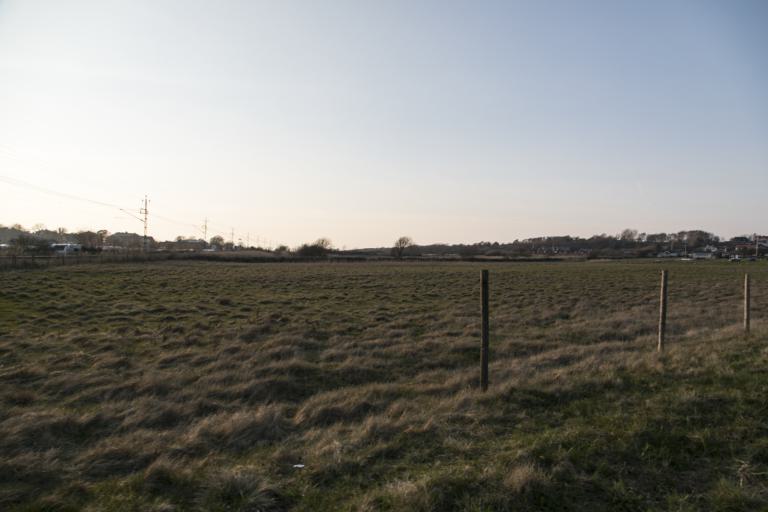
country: SE
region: Halland
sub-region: Varbergs Kommun
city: Varberg
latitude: 57.0861
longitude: 12.2534
